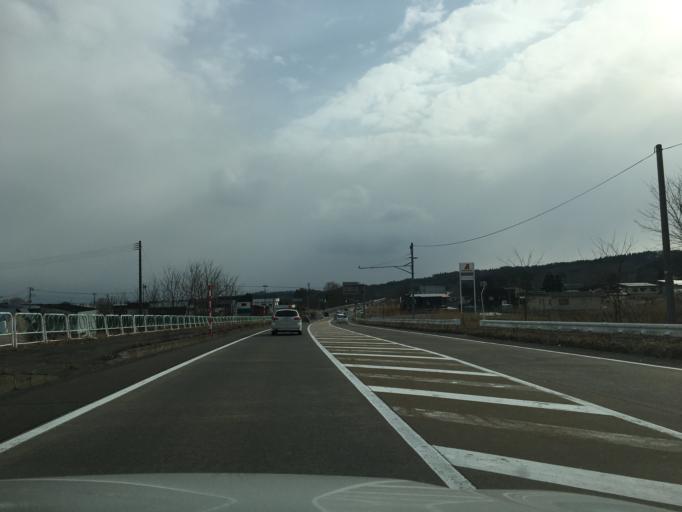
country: JP
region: Aomori
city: Namioka
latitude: 40.7587
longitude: 140.5867
